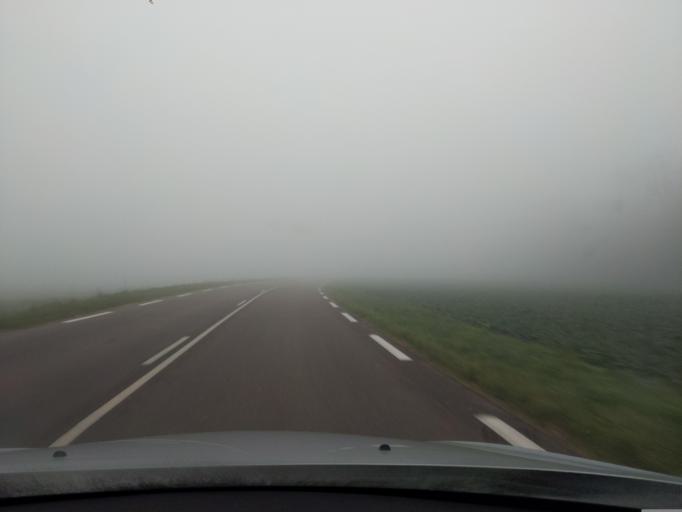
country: FR
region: Champagne-Ardenne
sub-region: Departement de la Haute-Marne
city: Langres
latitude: 47.8097
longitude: 5.2671
